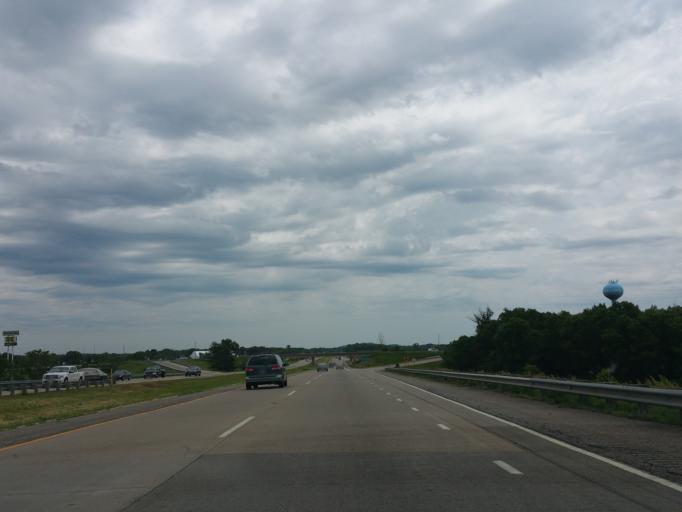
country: US
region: Wisconsin
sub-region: Juneau County
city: New Lisbon
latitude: 43.8850
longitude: -90.1516
